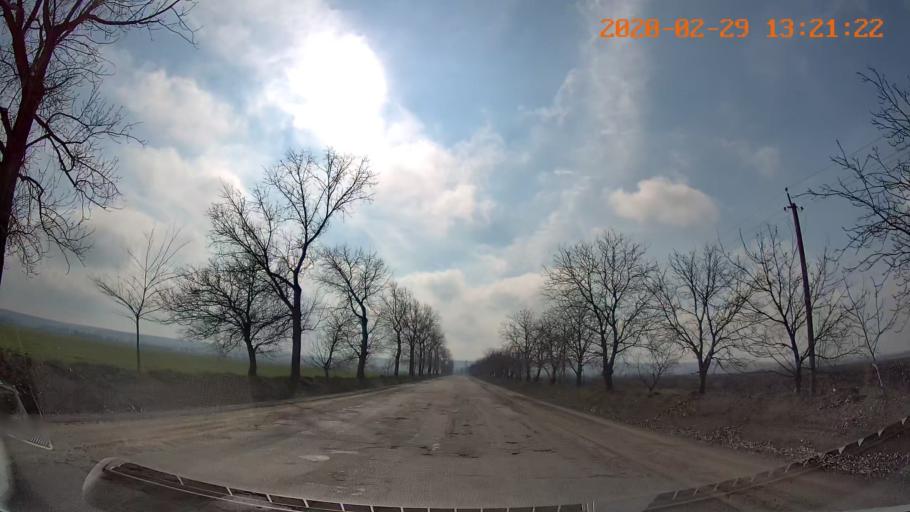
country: MD
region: Telenesti
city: Camenca
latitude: 47.9708
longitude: 28.6335
